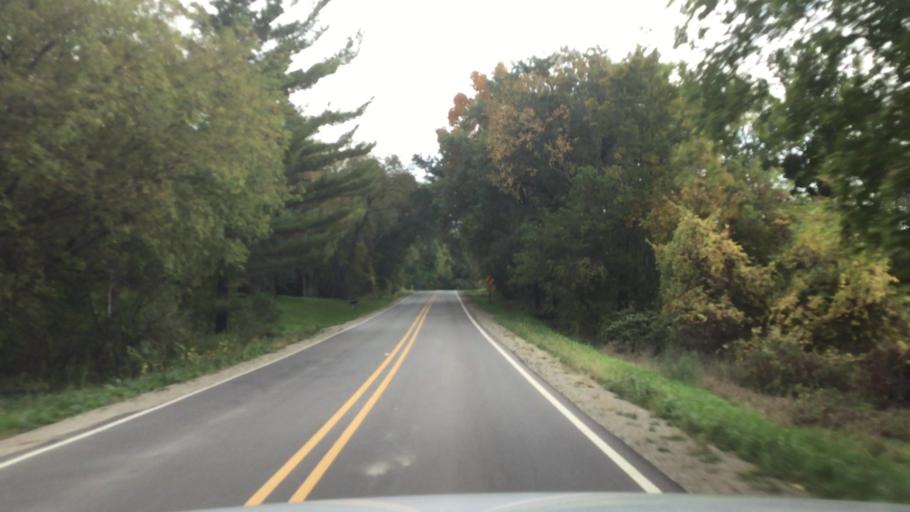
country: US
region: Michigan
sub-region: Genesee County
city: Fenton
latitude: 42.6986
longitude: -83.7028
